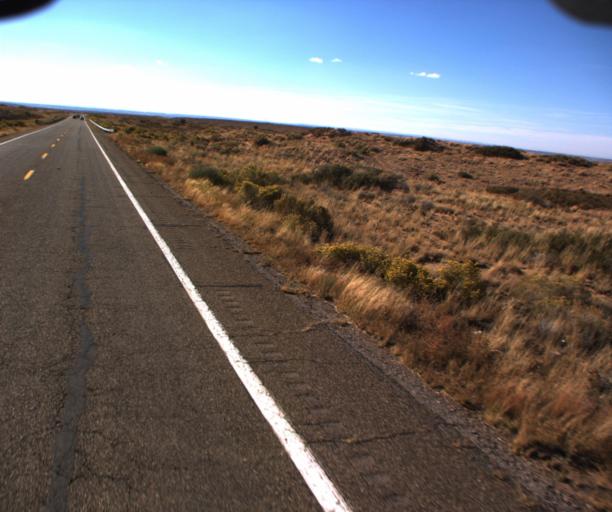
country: US
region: Arizona
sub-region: Coconino County
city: Kaibito
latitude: 36.6129
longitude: -111.0082
